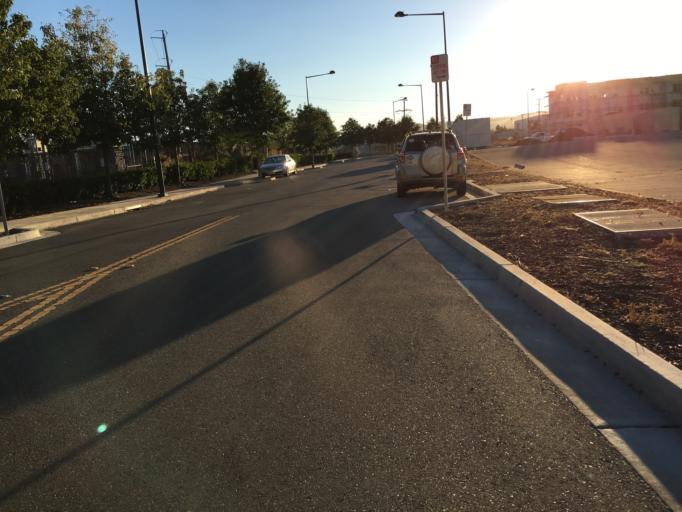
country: US
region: California
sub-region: Alameda County
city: Dublin
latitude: 37.7043
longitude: -121.9002
